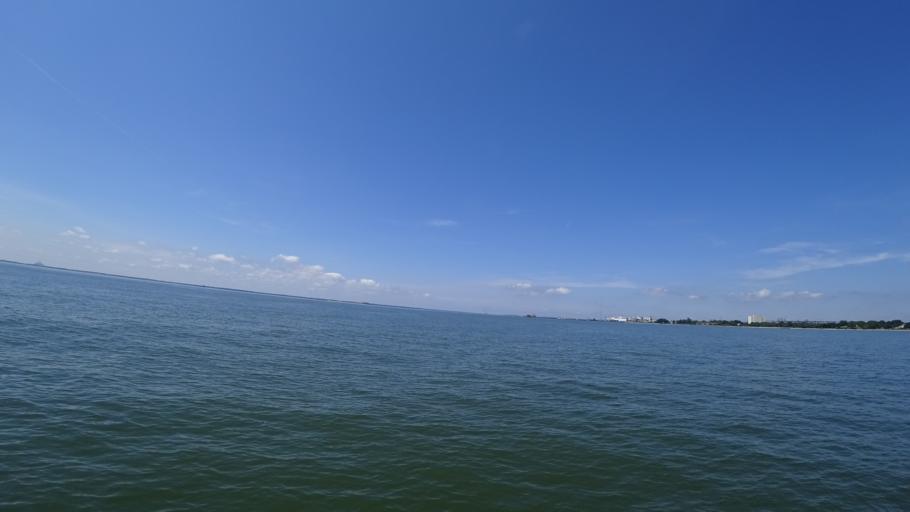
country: US
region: Virginia
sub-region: City of Newport News
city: Newport News
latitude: 36.9728
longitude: -76.3912
